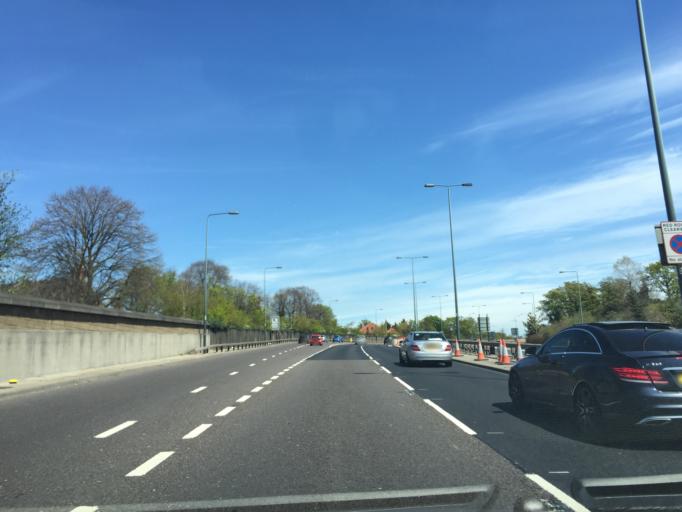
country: GB
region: England
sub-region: Greater London
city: Walthamstow
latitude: 51.5717
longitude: 0.0111
